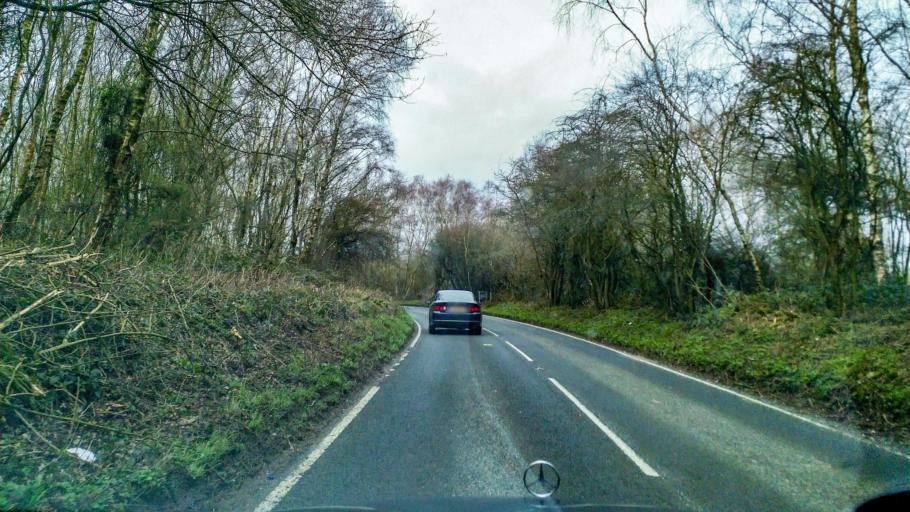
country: GB
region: England
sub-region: Surrey
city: Chilworth
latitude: 51.2384
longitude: -0.5141
